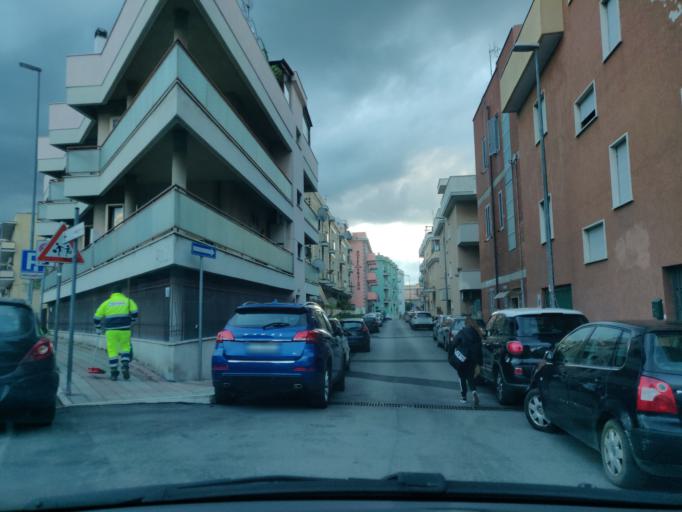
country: IT
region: Latium
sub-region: Citta metropolitana di Roma Capitale
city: Civitavecchia
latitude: 42.0947
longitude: 11.8041
